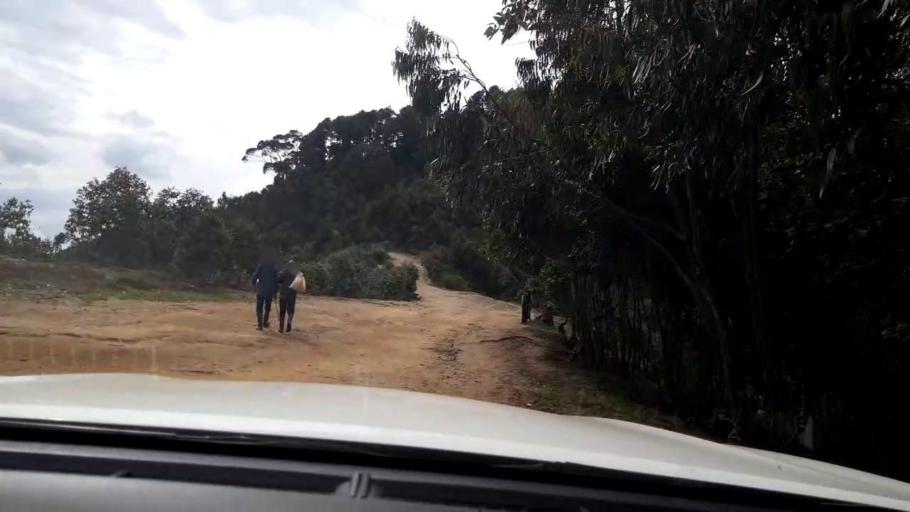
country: RW
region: Western Province
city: Kibuye
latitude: -1.8782
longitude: 29.4551
